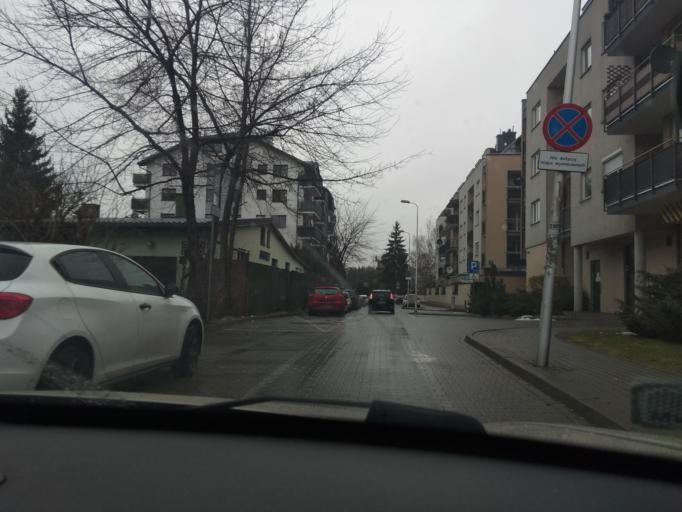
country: PL
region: Masovian Voivodeship
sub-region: Powiat pruszkowski
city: Piastow
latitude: 52.1838
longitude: 20.8374
